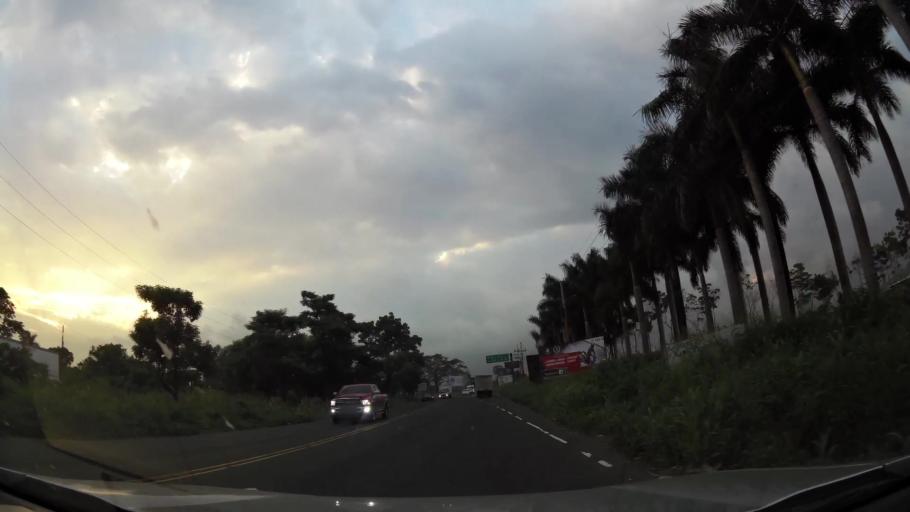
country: GT
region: Escuintla
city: Siquinala
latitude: 14.2973
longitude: -90.9491
